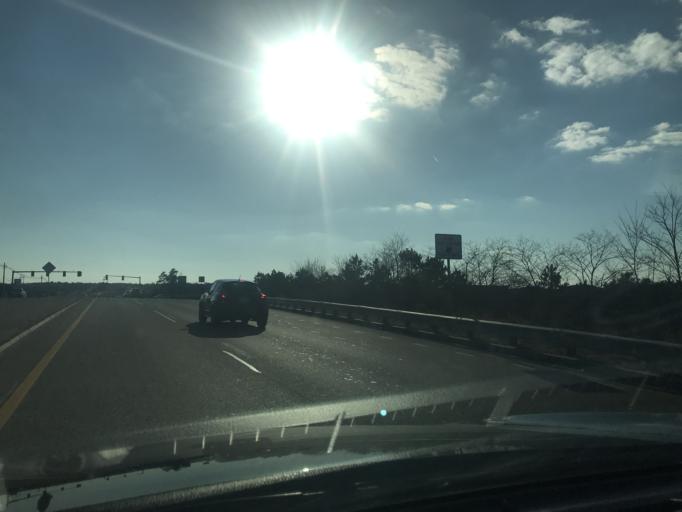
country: US
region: Massachusetts
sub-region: Plymouth County
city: North Plymouth
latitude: 41.9579
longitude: -70.7106
